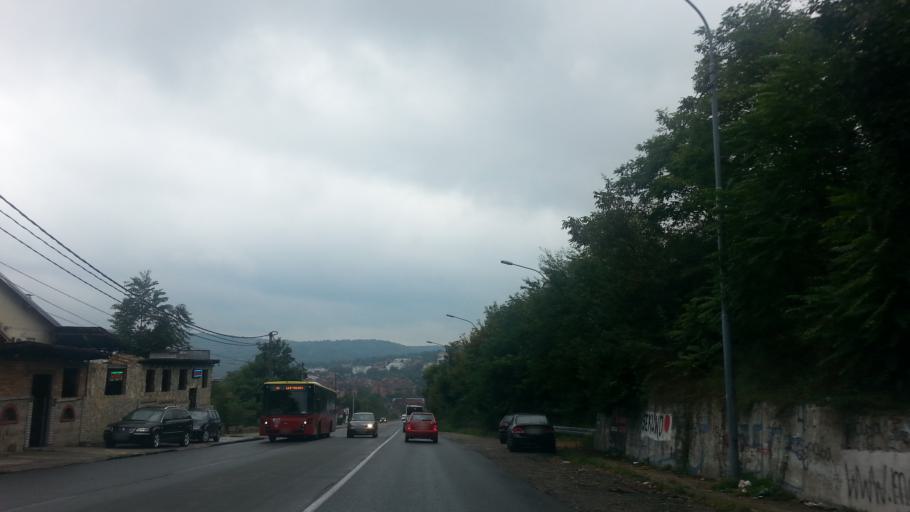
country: RS
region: Central Serbia
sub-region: Belgrade
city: Vozdovac
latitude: 44.7552
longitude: 20.4664
